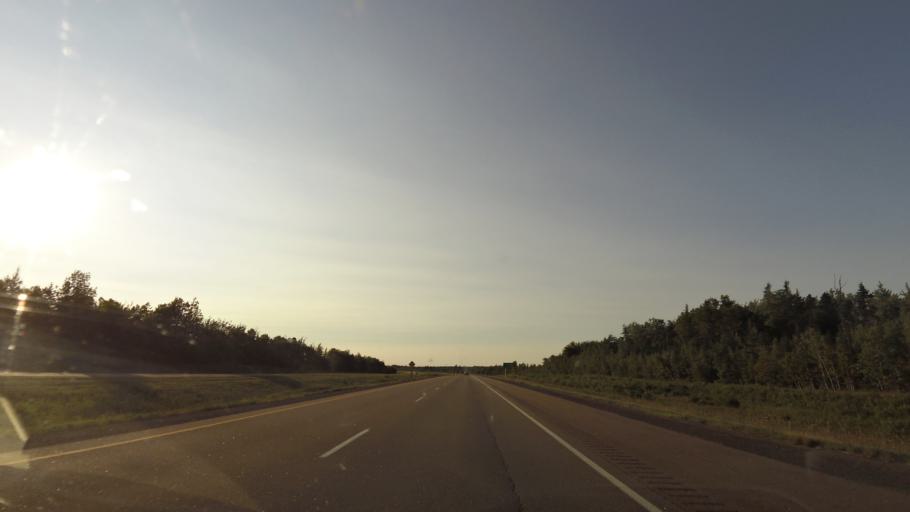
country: CA
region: New Brunswick
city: Dieppe
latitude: 46.1217
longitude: -64.6315
